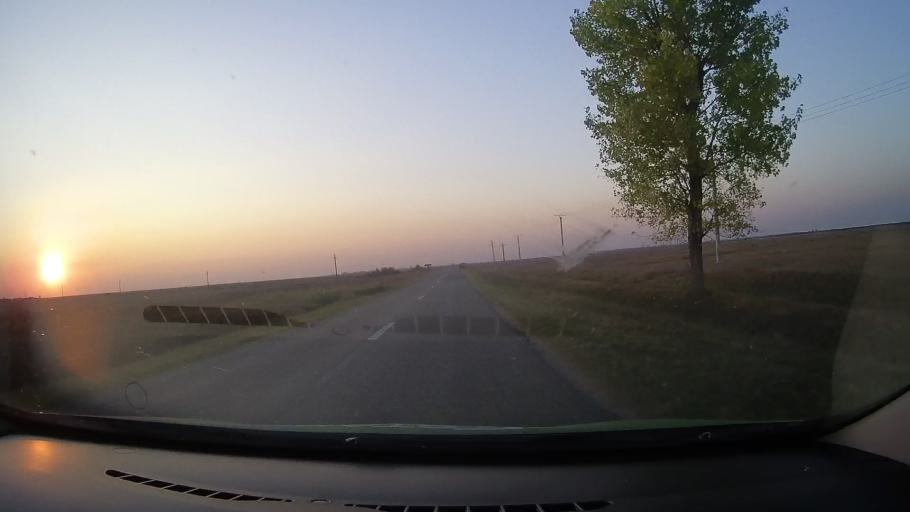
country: RO
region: Arad
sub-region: Comuna Zarand
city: Zarand
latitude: 46.4207
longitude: 21.6145
